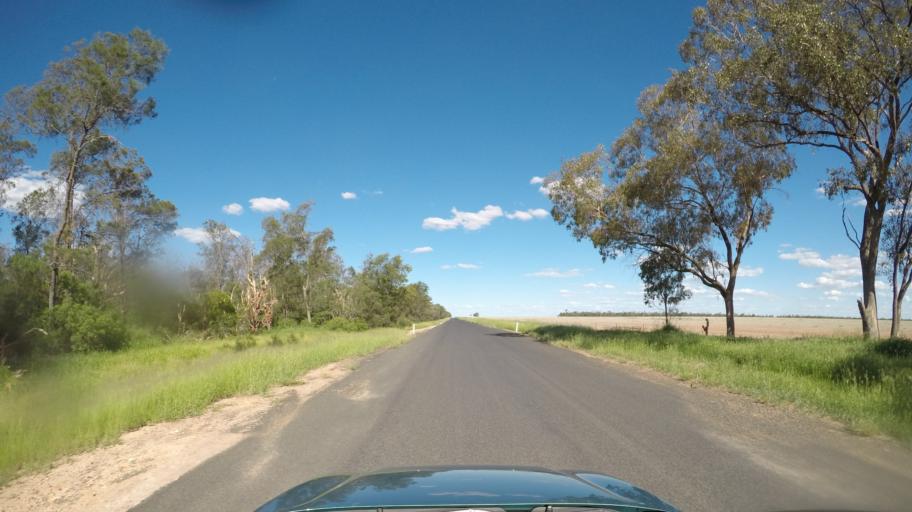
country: AU
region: Queensland
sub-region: Goondiwindi
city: Goondiwindi
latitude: -28.1573
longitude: 150.3843
